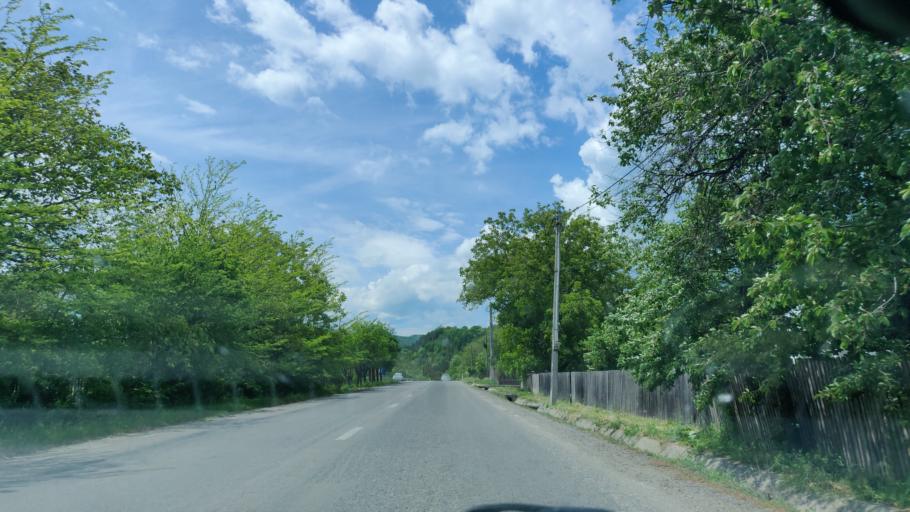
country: RO
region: Vrancea
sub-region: Comuna Vidra
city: Vidra
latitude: 45.8963
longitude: 26.8578
